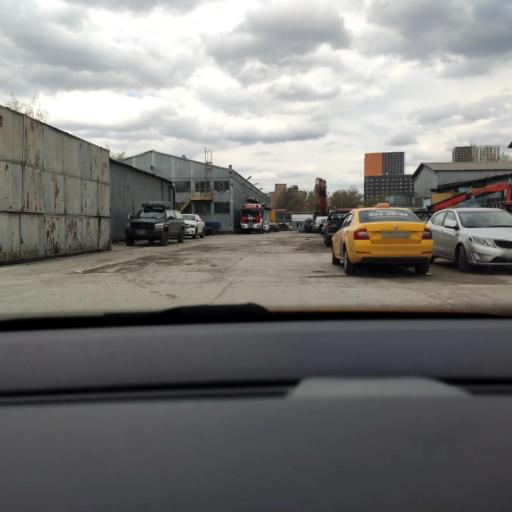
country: RU
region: Moscow
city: Kozeyevo
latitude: 55.8842
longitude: 37.6285
